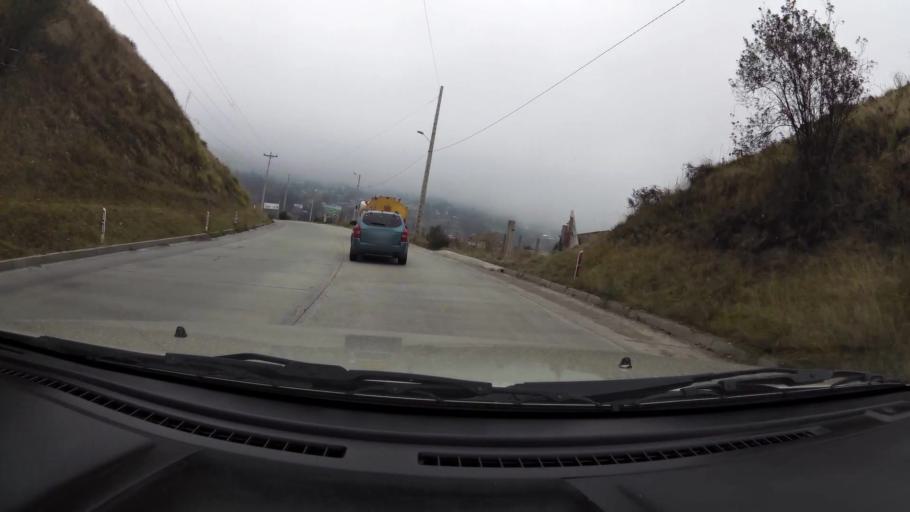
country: EC
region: Canar
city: Canar
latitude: -2.5628
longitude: -78.9289
